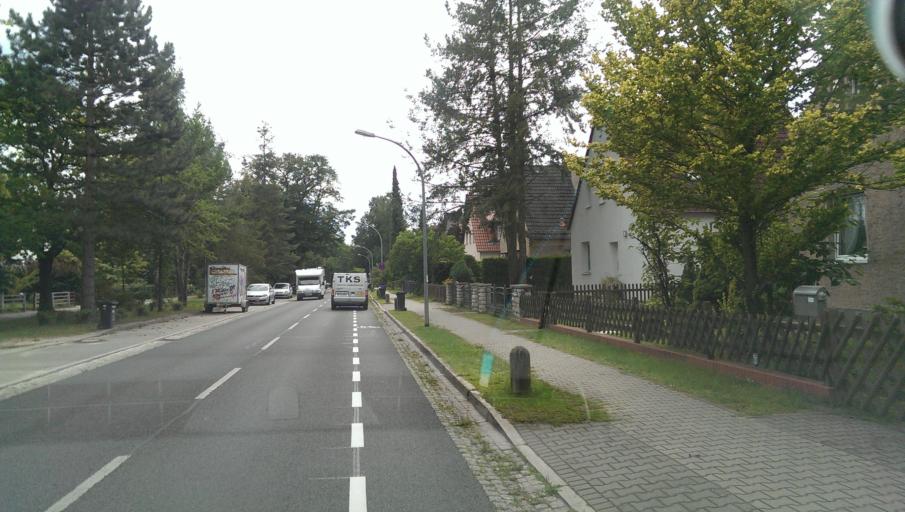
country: DE
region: Brandenburg
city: Kleinmachnow
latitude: 52.4084
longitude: 13.2176
